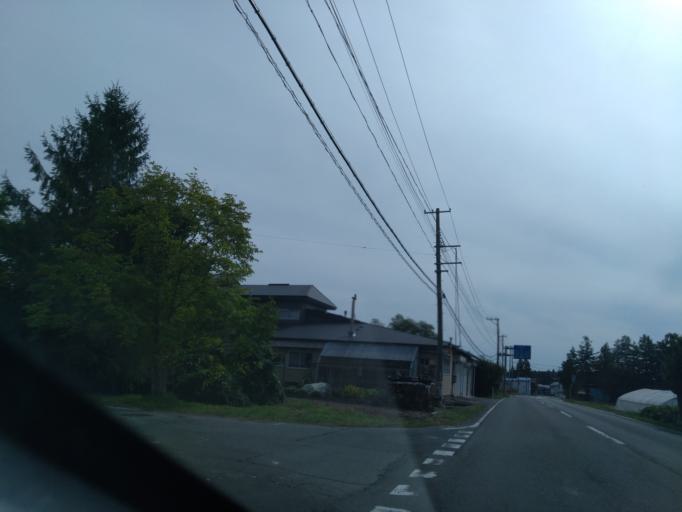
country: JP
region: Iwate
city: Hanamaki
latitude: 39.4273
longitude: 141.0844
